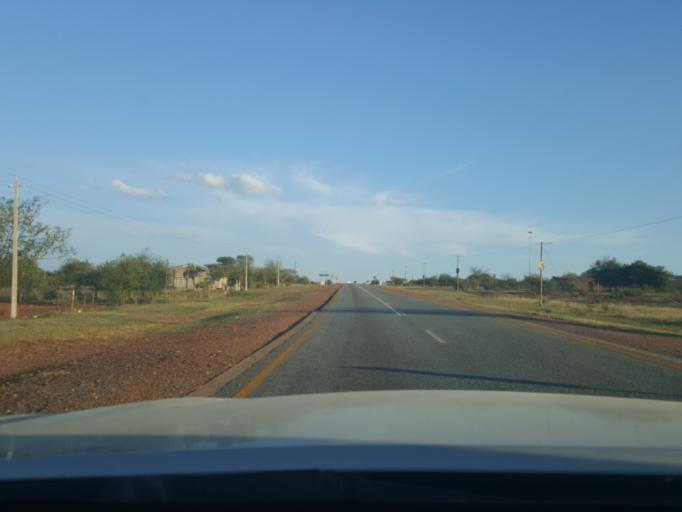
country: ZA
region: North-West
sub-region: Ngaka Modiri Molema District Municipality
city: Zeerust
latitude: -25.3820
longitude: 26.0831
